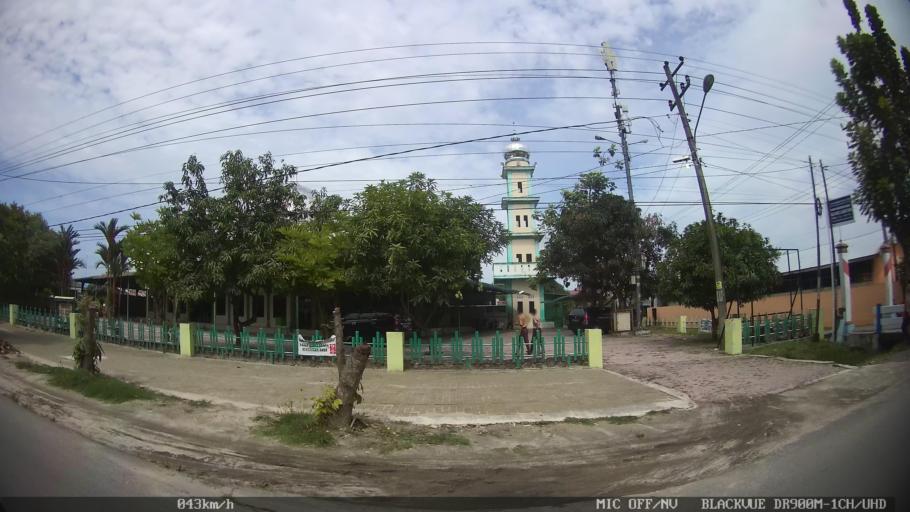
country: ID
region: North Sumatra
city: Percut
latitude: 3.6090
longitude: 98.8076
